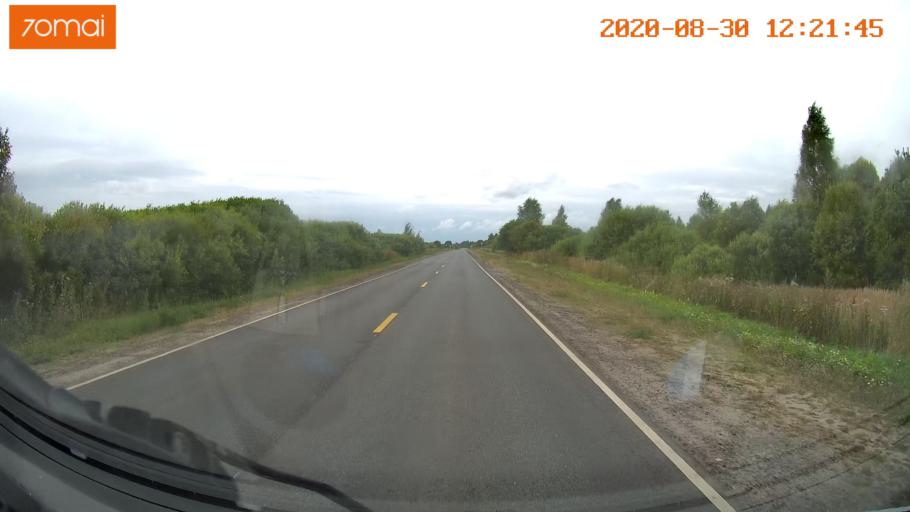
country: RU
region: Ivanovo
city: Yur'yevets
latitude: 57.3265
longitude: 42.8679
